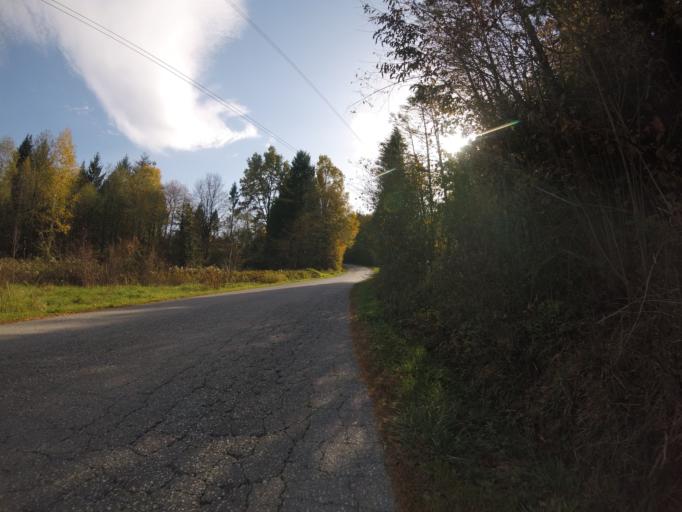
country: HR
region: Zagrebacka
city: Mraclin
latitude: 45.6231
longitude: 16.0713
